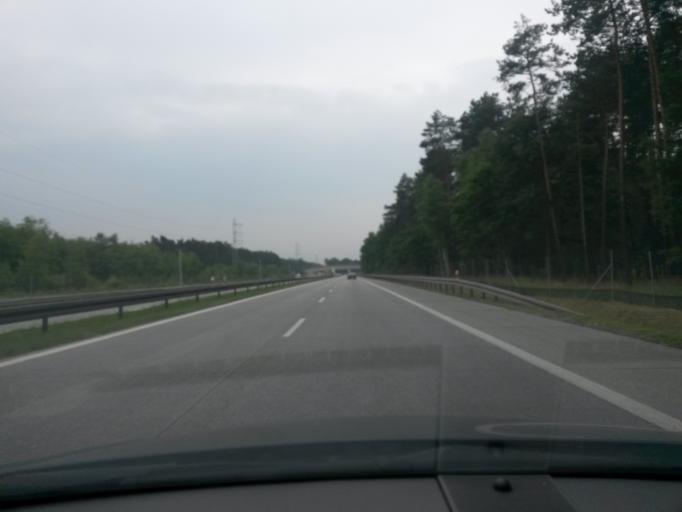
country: PL
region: Lodz Voivodeship
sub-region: Powiat piotrkowski
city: Moszczenica
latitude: 51.4535
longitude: 19.7705
